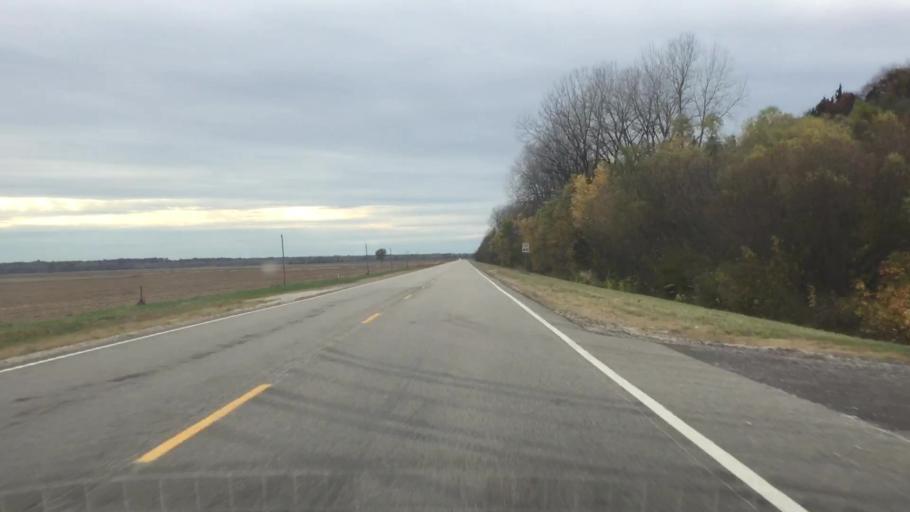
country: US
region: Missouri
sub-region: Callaway County
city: Holts Summit
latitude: 38.5821
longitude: -92.0668
